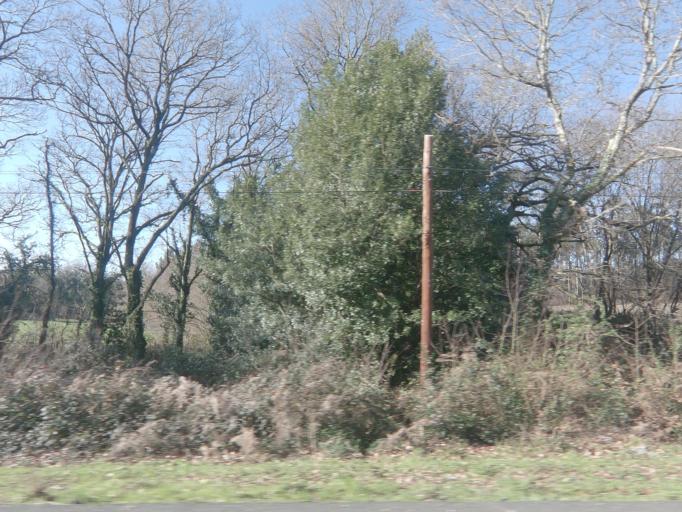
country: ES
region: Galicia
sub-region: Provincia da Coruna
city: Vedra
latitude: 42.8071
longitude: -8.4778
